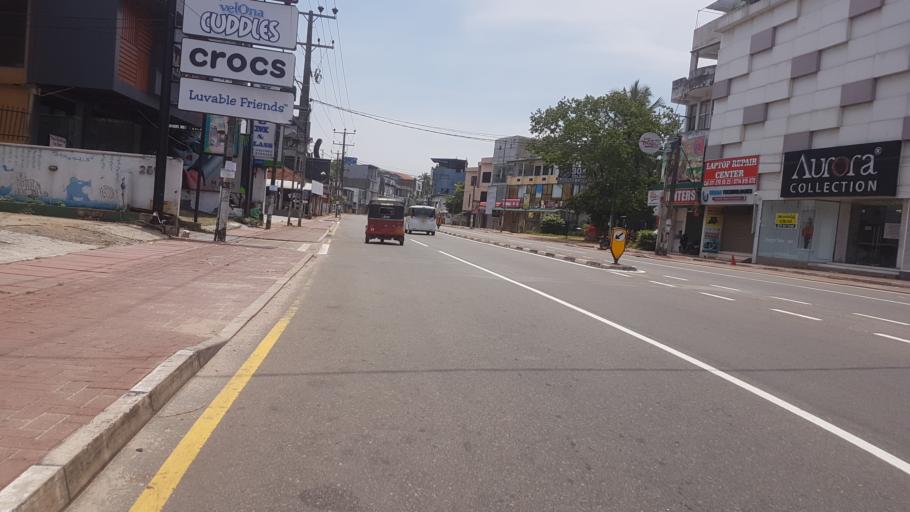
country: LK
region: Western
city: Battaramulla South
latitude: 6.8935
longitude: 79.9260
